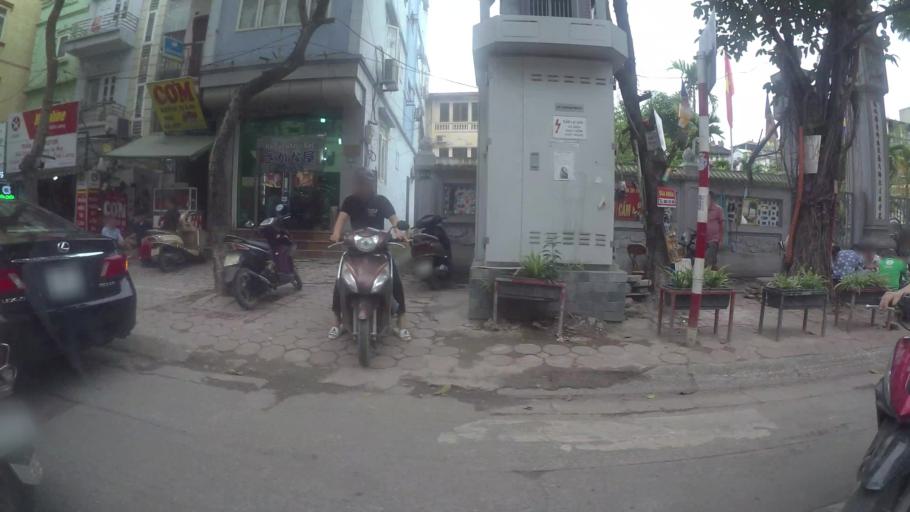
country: VN
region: Ha Noi
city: Dong Da
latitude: 21.0352
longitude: 105.8223
